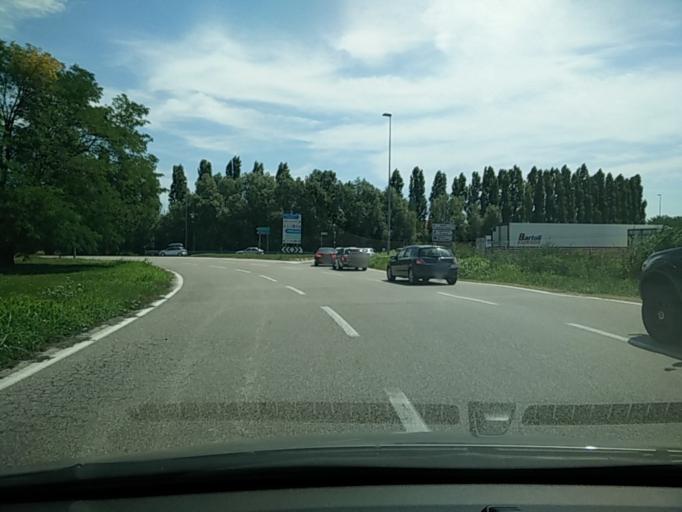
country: IT
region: Veneto
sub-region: Provincia di Venezia
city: Iesolo
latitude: 45.5401
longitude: 12.6269
